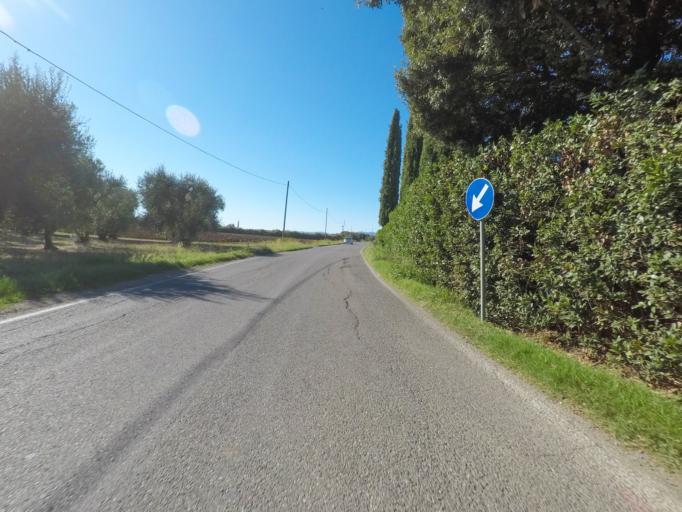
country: IT
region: Tuscany
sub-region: Provincia di Grosseto
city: Grosseto
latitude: 42.7699
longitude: 11.1408
